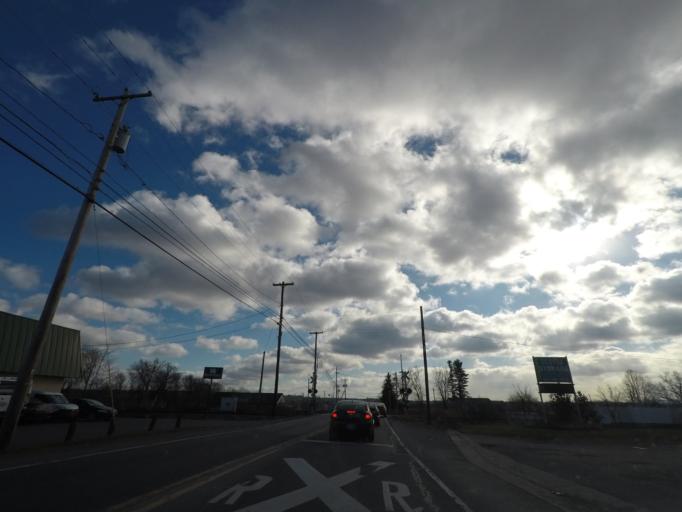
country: US
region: New York
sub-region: Schenectady County
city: Schenectady
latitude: 42.8412
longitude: -73.9392
